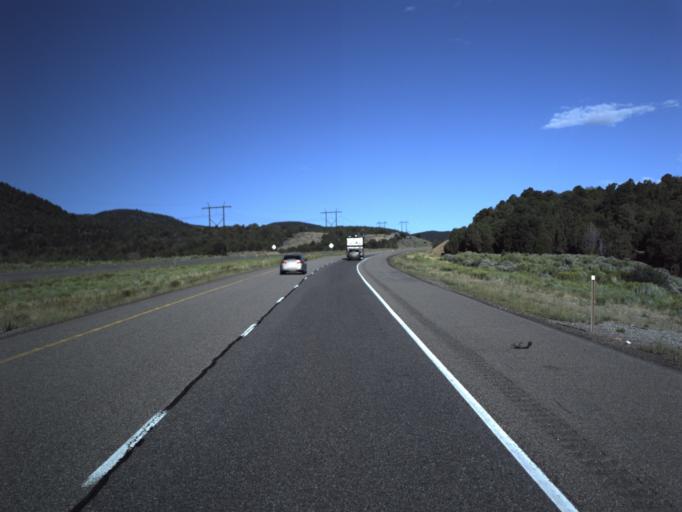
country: US
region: Utah
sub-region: Beaver County
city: Beaver
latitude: 38.5741
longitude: -112.4636
